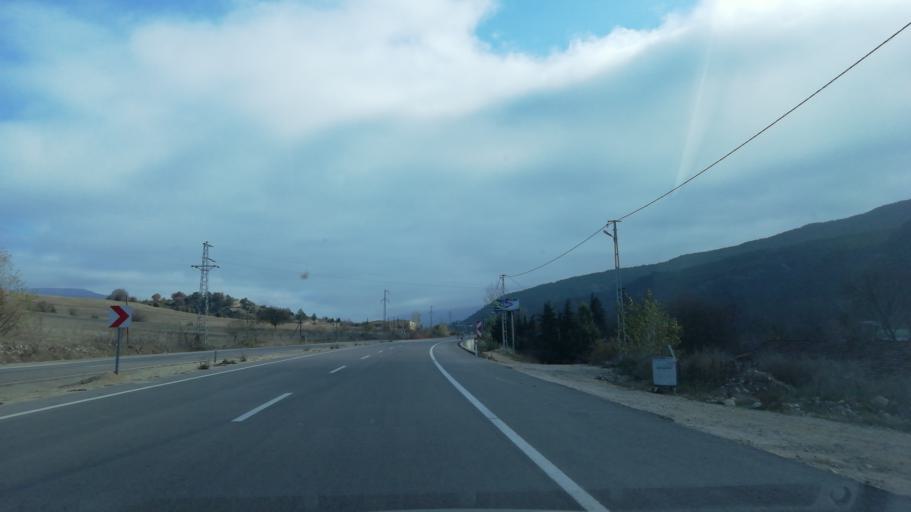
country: TR
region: Karabuk
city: Safranbolu
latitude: 41.2180
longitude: 32.7473
